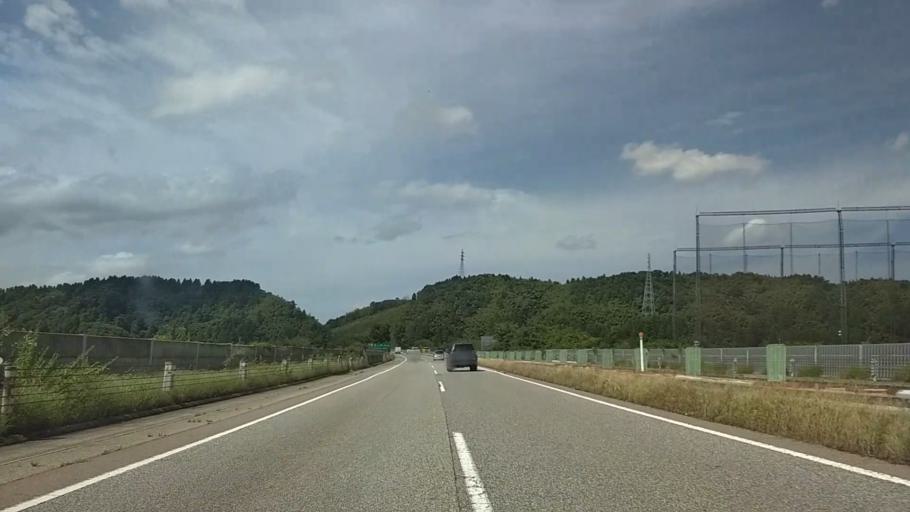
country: JP
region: Toyama
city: Kuragaki-kosugi
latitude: 36.6796
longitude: 137.1560
